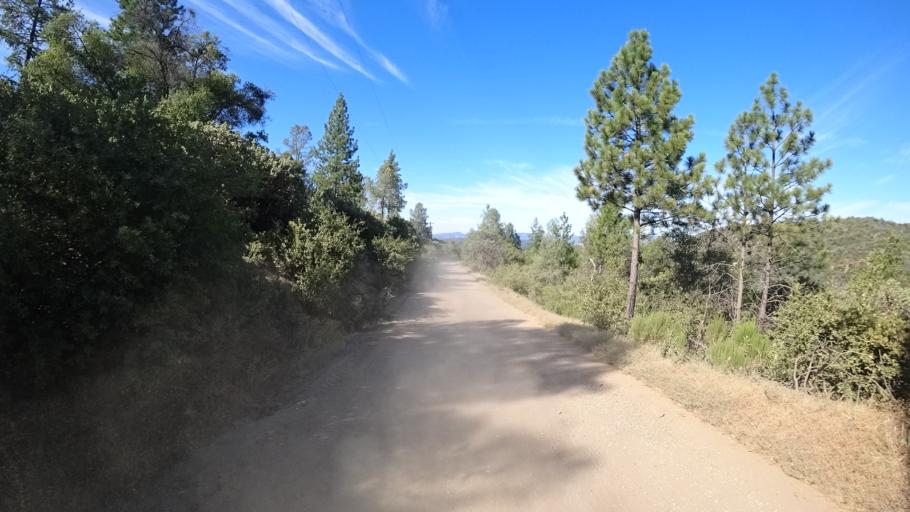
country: US
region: California
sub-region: Calaveras County
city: Mountain Ranch
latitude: 38.1767
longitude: -120.5249
